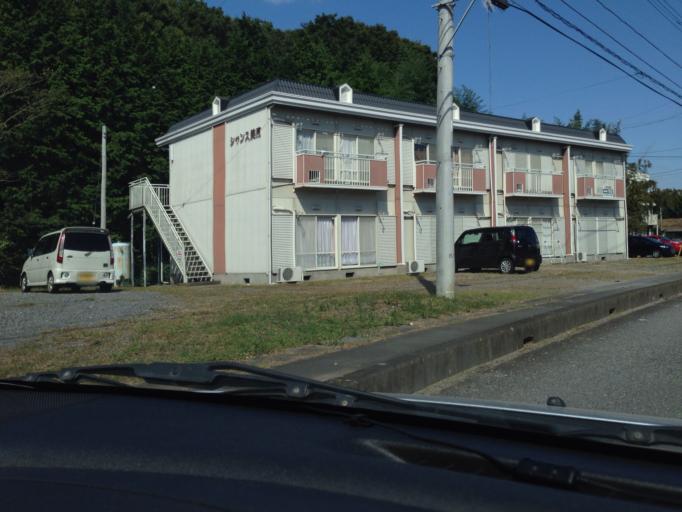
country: JP
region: Ibaraki
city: Inashiki
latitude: 36.0149
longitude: 140.3008
